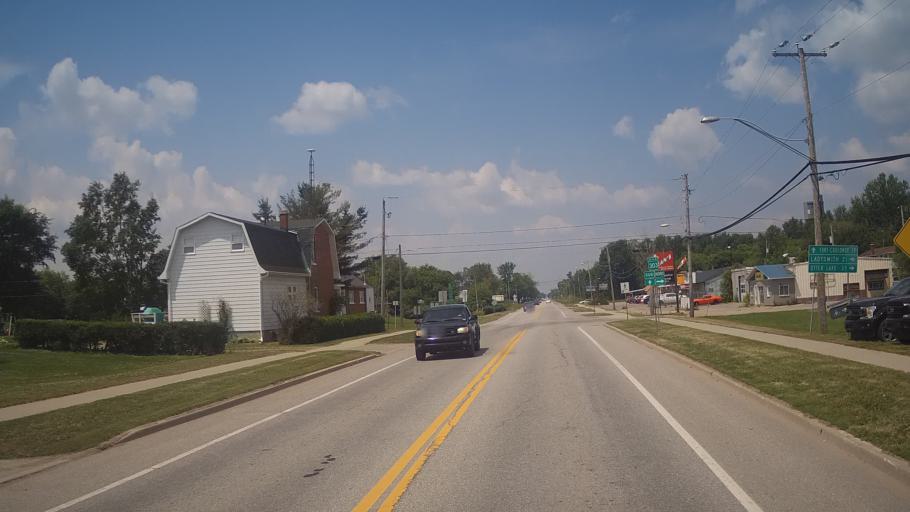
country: CA
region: Quebec
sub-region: Outaouais
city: Shawville
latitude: 45.5996
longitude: -76.4936
